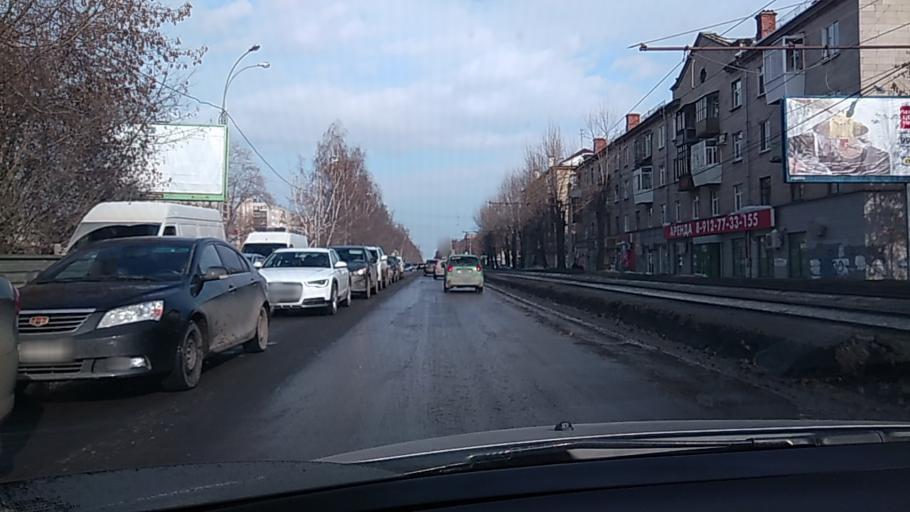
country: RU
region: Sverdlovsk
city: Yekaterinburg
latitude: 56.8524
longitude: 60.6434
